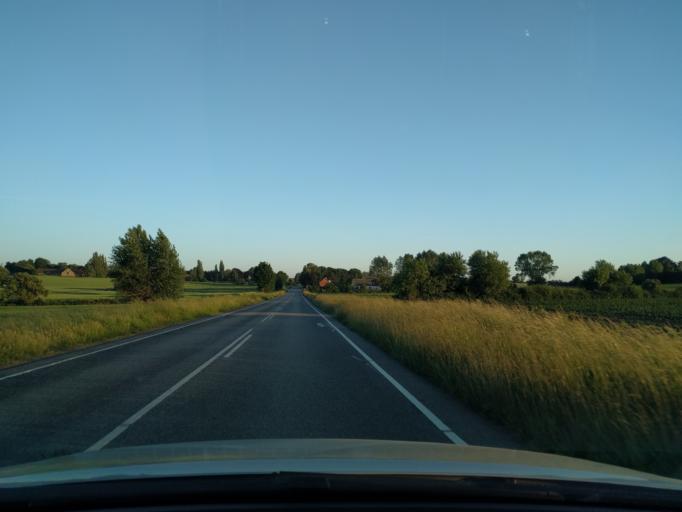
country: DK
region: South Denmark
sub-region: Kerteminde Kommune
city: Munkebo
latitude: 55.4731
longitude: 10.6021
